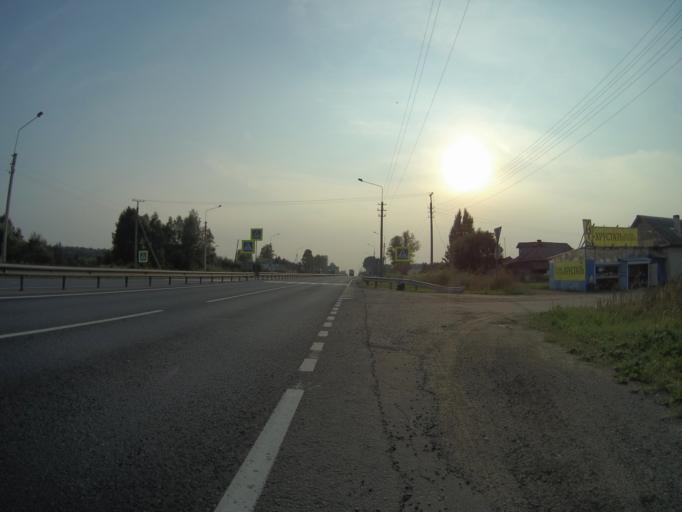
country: RU
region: Vladimir
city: Novki
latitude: 56.2019
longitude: 41.1058
